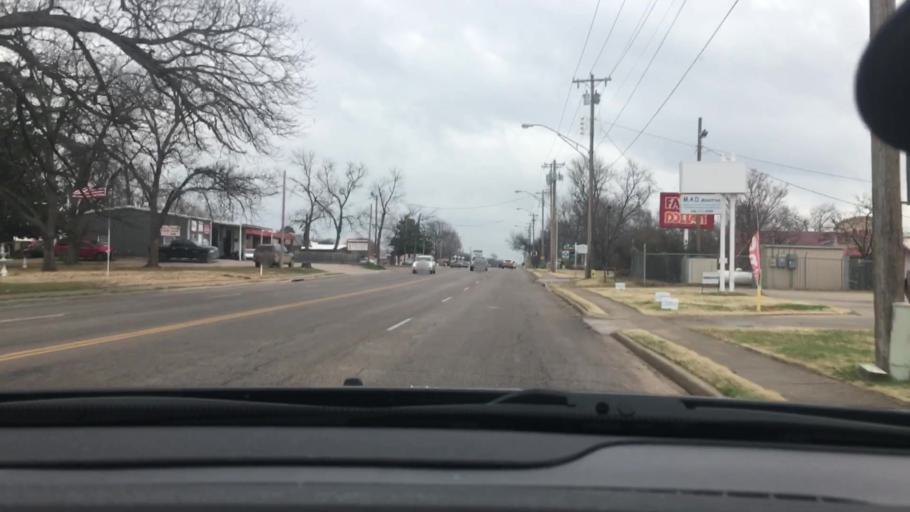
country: US
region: Oklahoma
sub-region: Johnston County
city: Tishomingo
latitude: 34.2306
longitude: -96.6680
